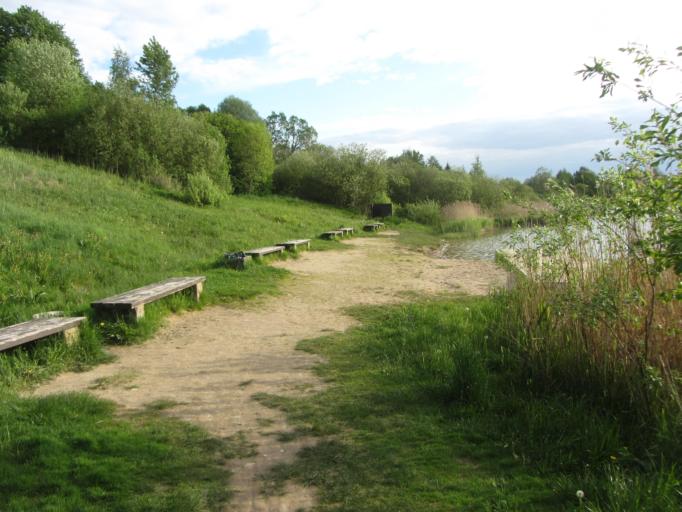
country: LT
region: Utenos apskritis
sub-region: Utena
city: Utena
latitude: 55.4919
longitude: 25.5939
